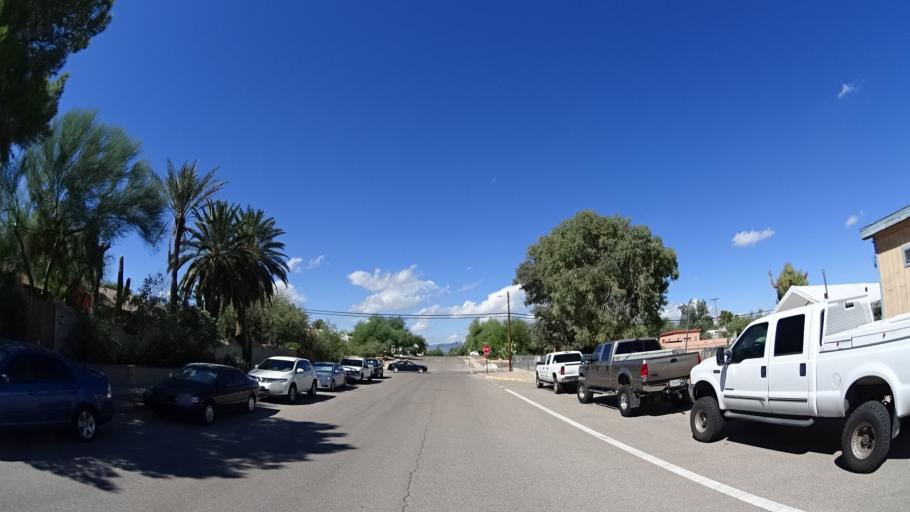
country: US
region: Arizona
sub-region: Pima County
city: Tucson
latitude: 32.2468
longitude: -110.9462
